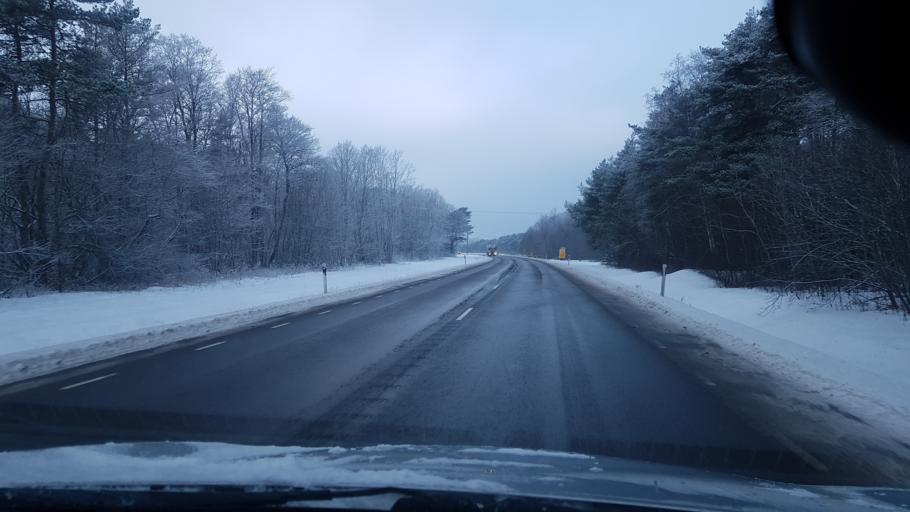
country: EE
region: Harju
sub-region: Paldiski linn
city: Paldiski
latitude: 59.3386
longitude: 24.2198
